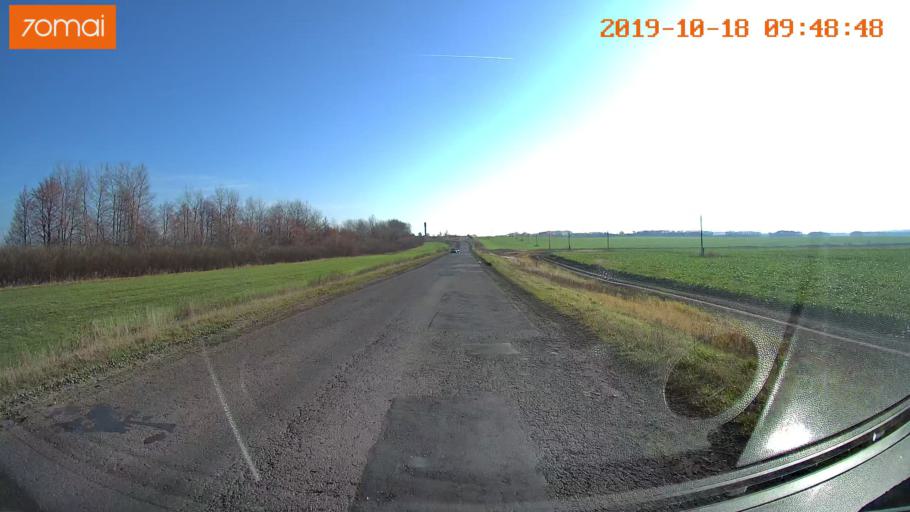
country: RU
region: Tula
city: Kazachka
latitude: 53.3168
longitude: 38.2575
